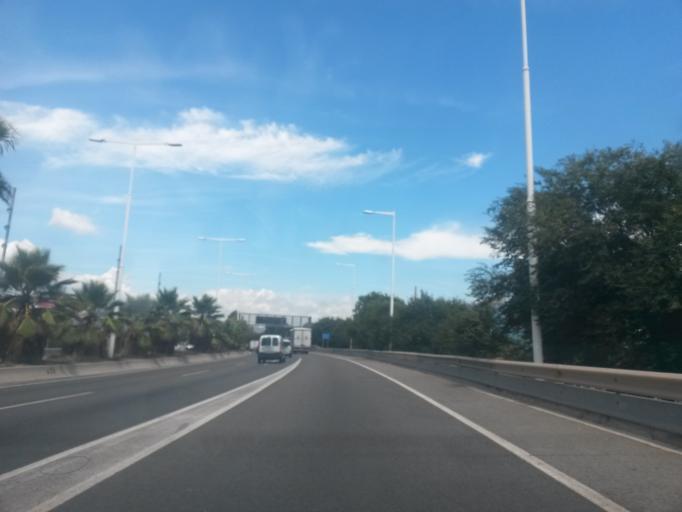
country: ES
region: Catalonia
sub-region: Provincia de Barcelona
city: Sant Adria de Besos
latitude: 41.4149
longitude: 2.2251
